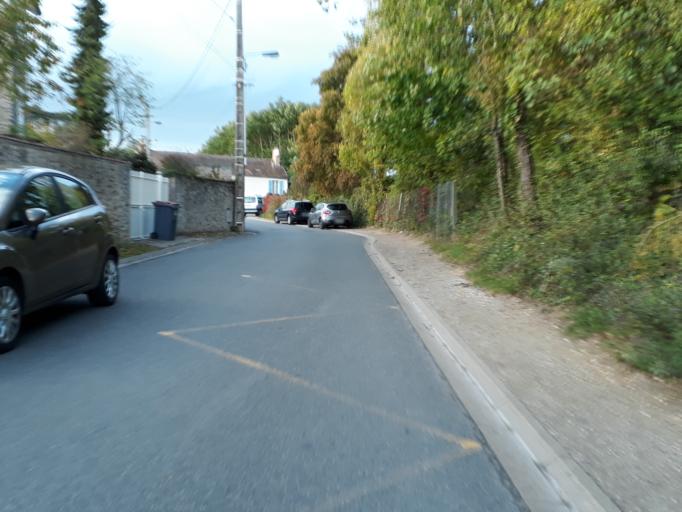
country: FR
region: Ile-de-France
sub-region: Departement de Seine-et-Marne
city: Bois-le-Roi
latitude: 48.4661
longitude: 2.7061
